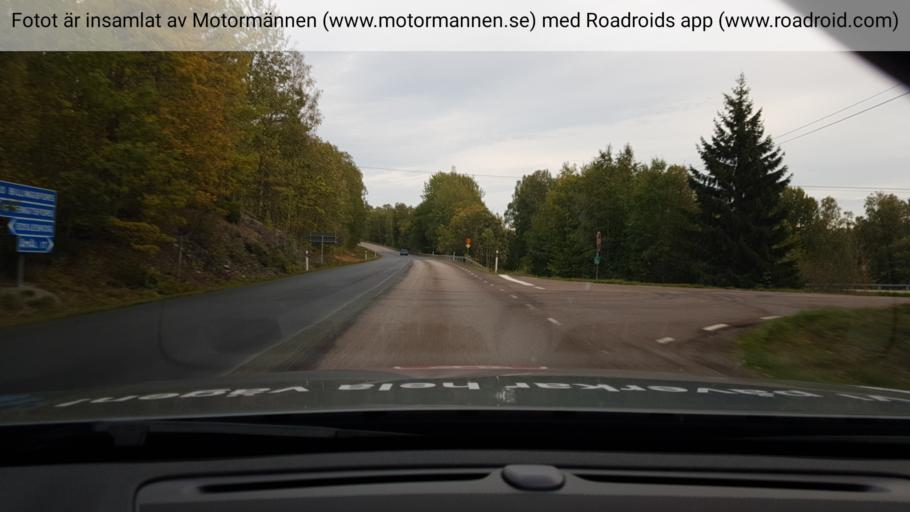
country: SE
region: Vaestra Goetaland
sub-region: Bengtsfors Kommun
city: Dals Langed
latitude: 59.0531
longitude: 12.4696
